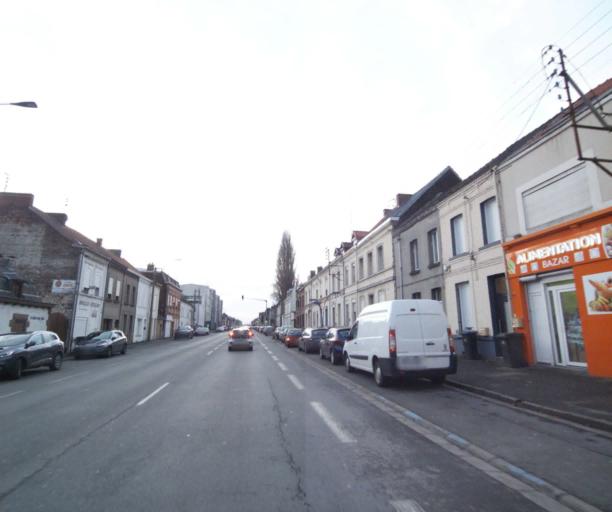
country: FR
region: Nord-Pas-de-Calais
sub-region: Departement du Nord
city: Beuvrages
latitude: 50.3784
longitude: 3.4960
